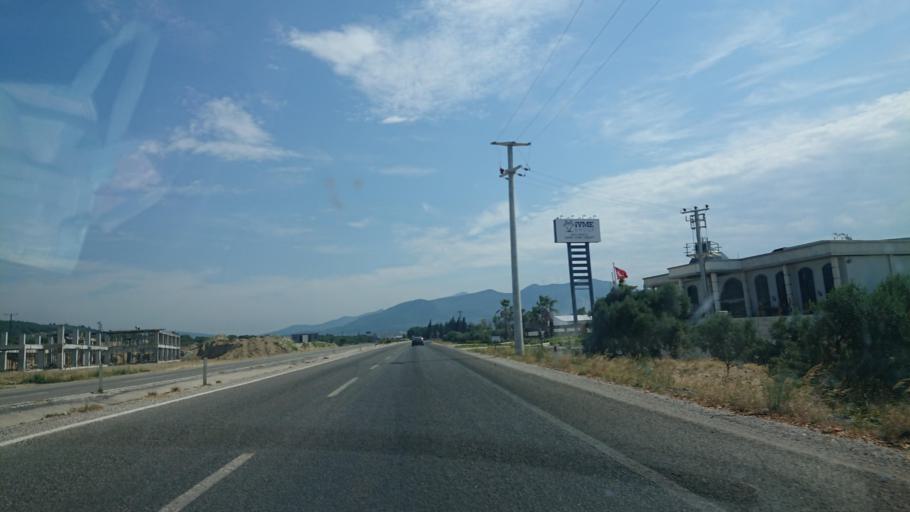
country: TR
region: Izmir
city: Dagkizilca
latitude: 38.2481
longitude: 27.3797
